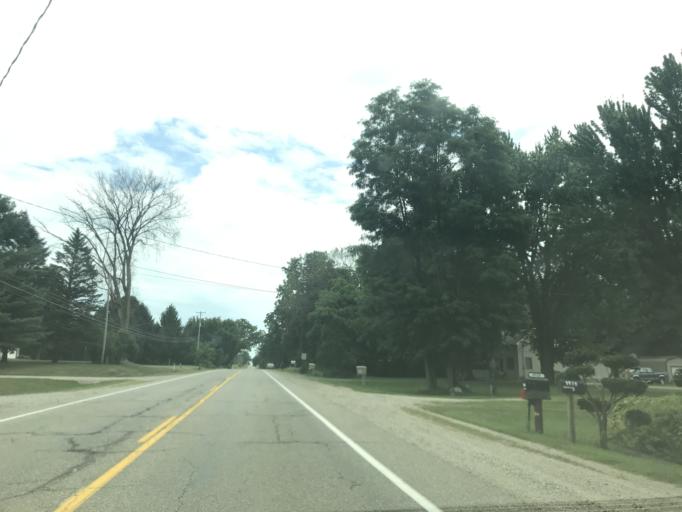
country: US
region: Michigan
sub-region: Clinton County
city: Wacousta
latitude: 42.7926
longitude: -84.7110
